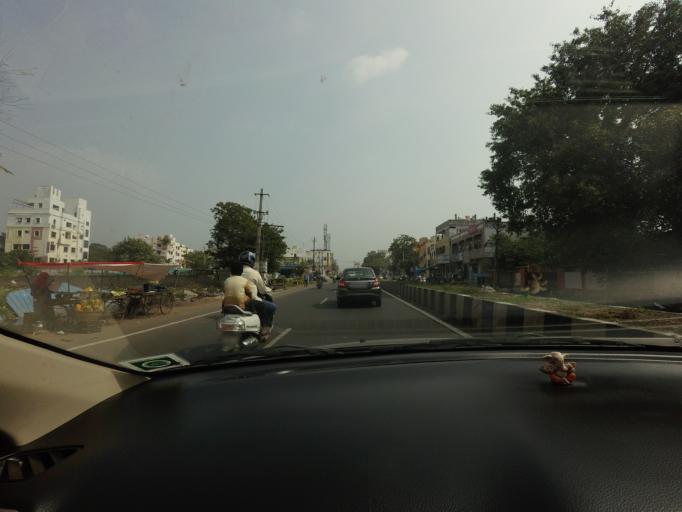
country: IN
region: Andhra Pradesh
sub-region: Krishna
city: Yanamalakuduru
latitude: 16.4846
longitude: 80.6844
